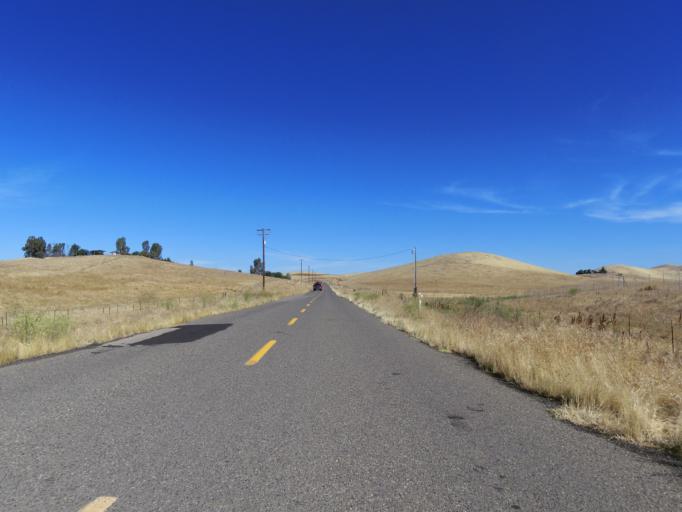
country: US
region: California
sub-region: Madera County
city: Bonadelle Ranchos-Madera Ranchos
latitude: 37.1152
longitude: -119.9215
